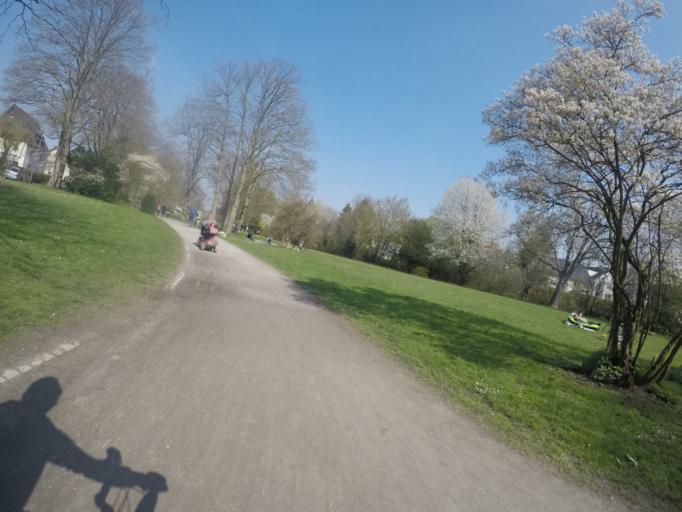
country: DE
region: North Rhine-Westphalia
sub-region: Regierungsbezirk Detmold
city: Bielefeld
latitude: 52.0232
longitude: 8.5678
